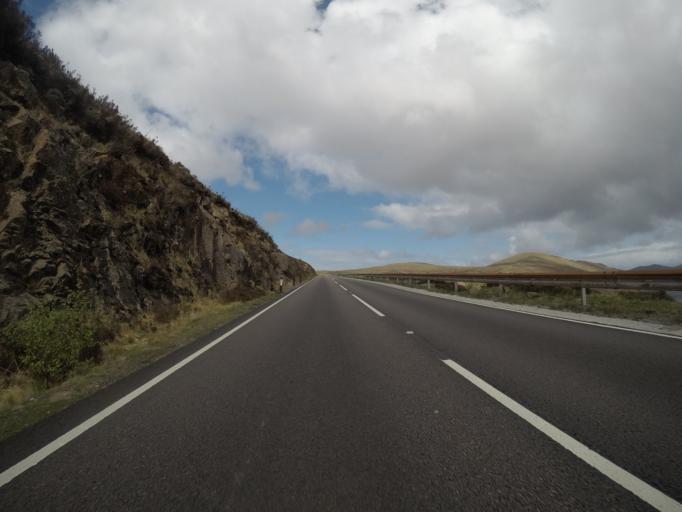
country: GB
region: Scotland
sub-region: Highland
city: Portree
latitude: 57.2705
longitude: -6.0894
